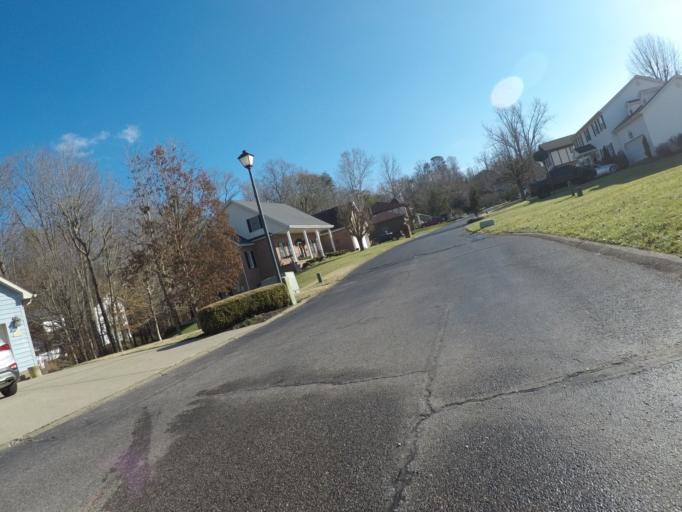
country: US
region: West Virginia
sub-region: Cabell County
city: Pea Ridge
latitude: 38.4184
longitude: -82.3254
